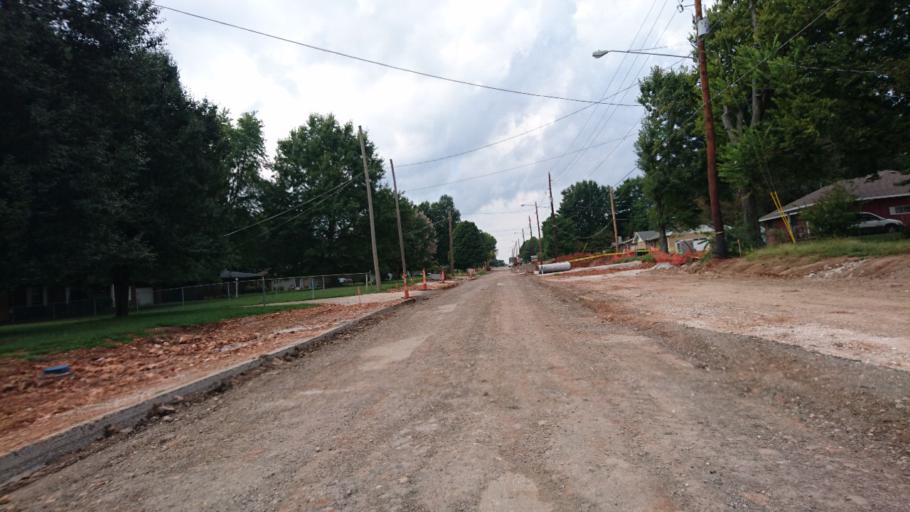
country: US
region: Missouri
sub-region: Greene County
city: Springfield
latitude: 37.2050
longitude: -93.3544
